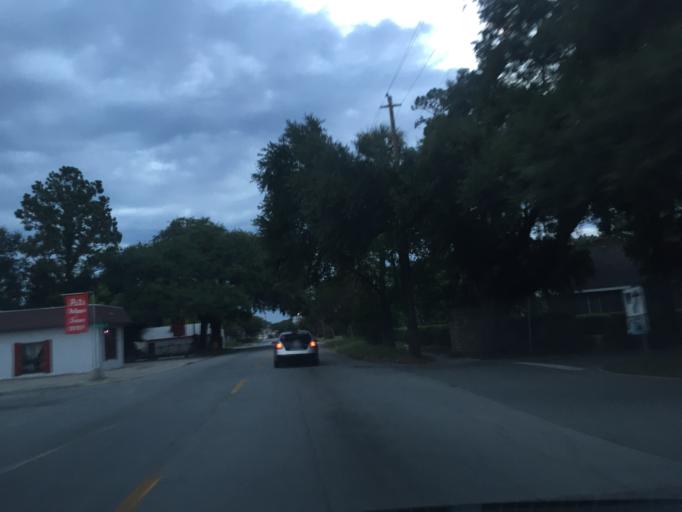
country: US
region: Georgia
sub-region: Chatham County
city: Savannah
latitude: 32.0398
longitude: -81.1070
